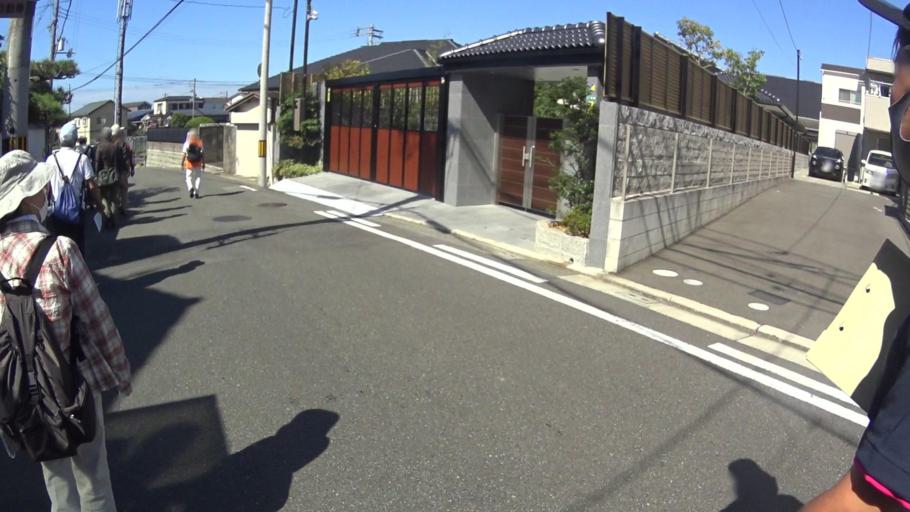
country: JP
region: Osaka
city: Takaishi
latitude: 34.5364
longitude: 135.4671
